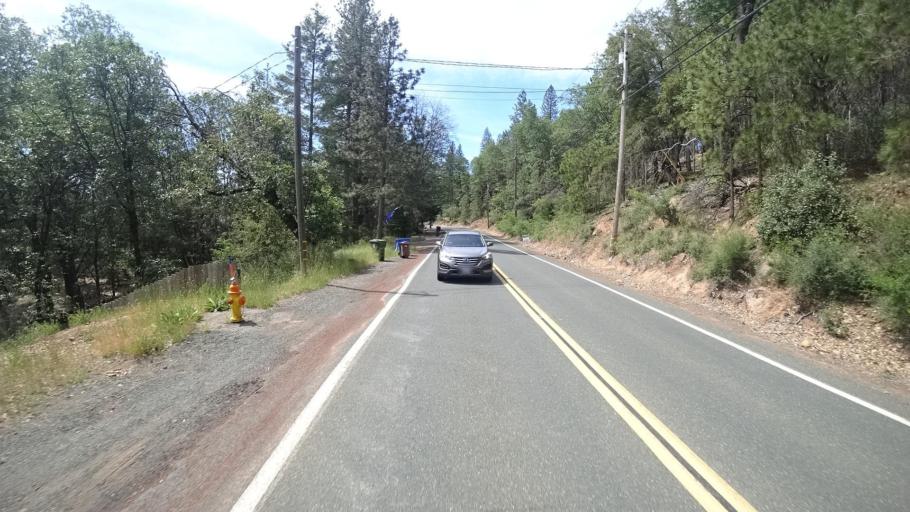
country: US
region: California
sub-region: Lake County
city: Cobb
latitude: 38.8587
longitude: -122.7004
